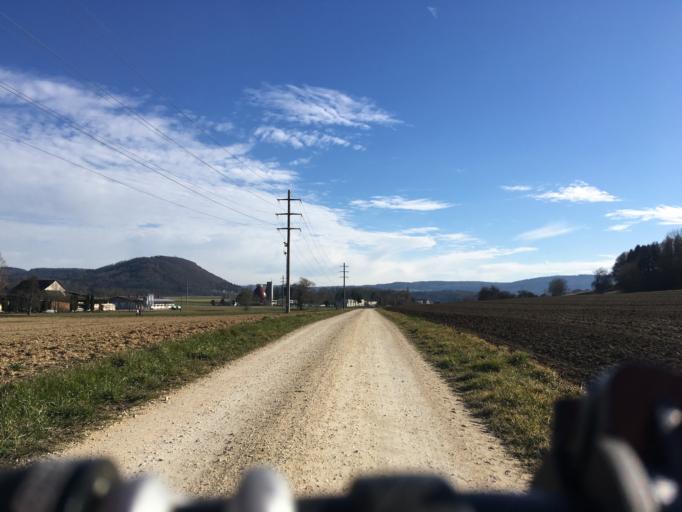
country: CH
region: Schaffhausen
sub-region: Bezirk Stein
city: Ramsen
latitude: 47.6979
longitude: 8.8106
